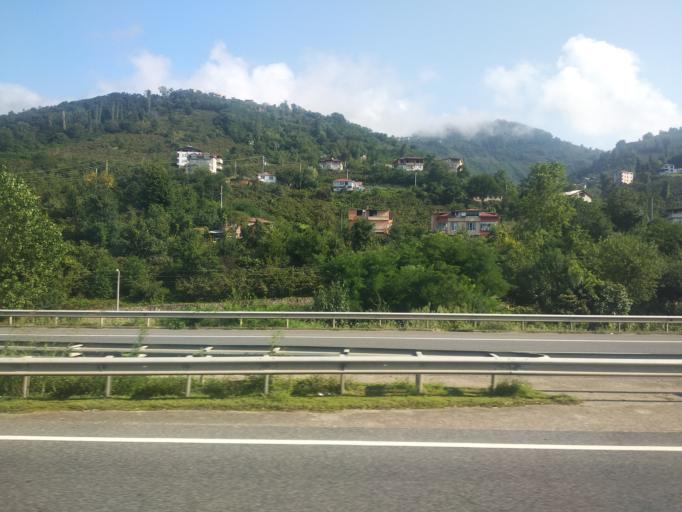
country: TR
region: Ordu
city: Ordu
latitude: 41.0161
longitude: 37.8425
